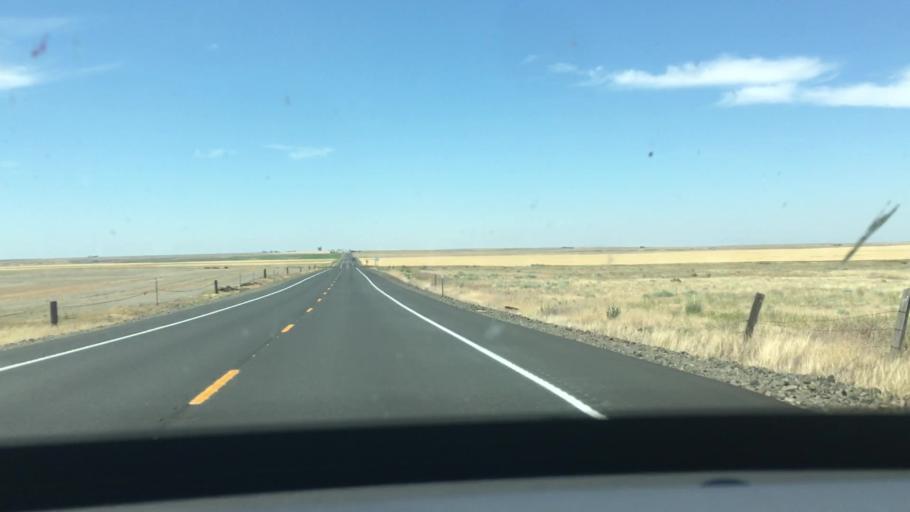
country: US
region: Oregon
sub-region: Sherman County
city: Moro
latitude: 45.1224
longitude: -120.6871
